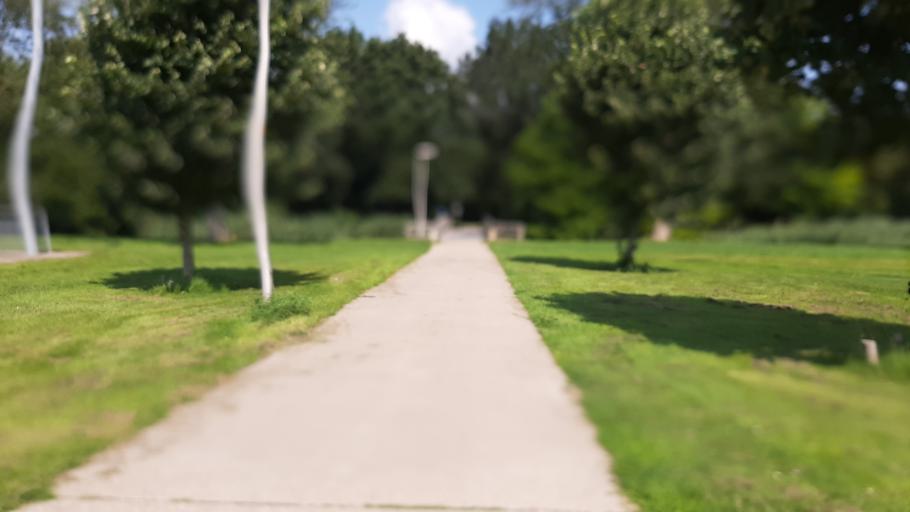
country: NL
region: Flevoland
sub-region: Gemeente Zeewolde
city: Zeewolde
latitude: 52.3280
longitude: 5.5241
